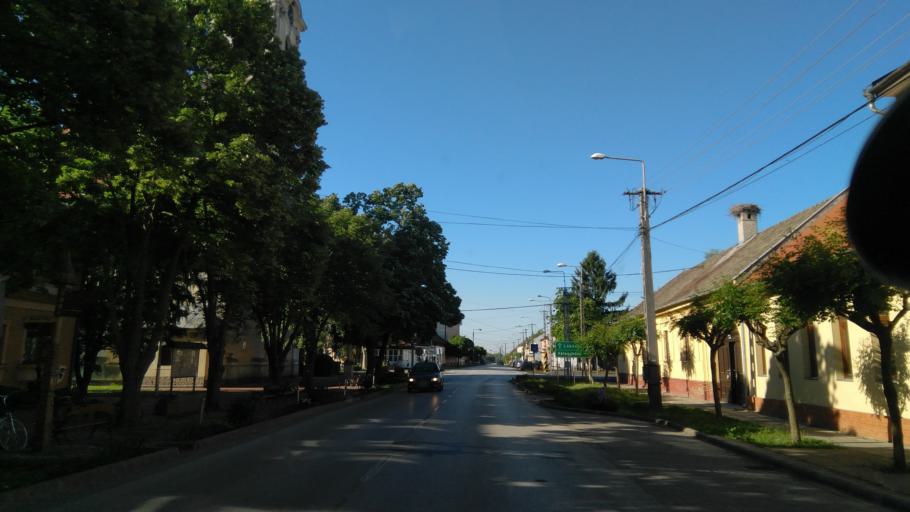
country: HU
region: Bekes
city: Elek
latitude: 46.5300
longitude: 21.2528
